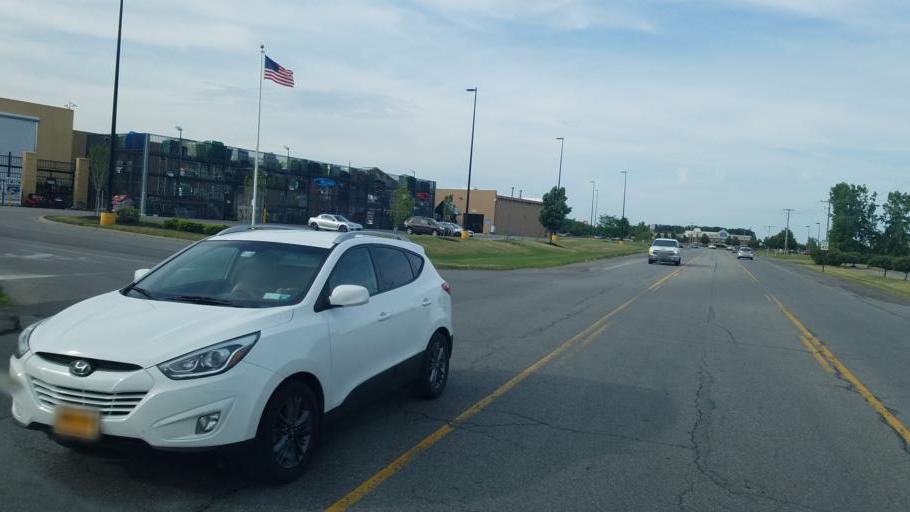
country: US
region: New York
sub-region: Genesee County
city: Batavia
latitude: 43.0121
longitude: -78.2077
